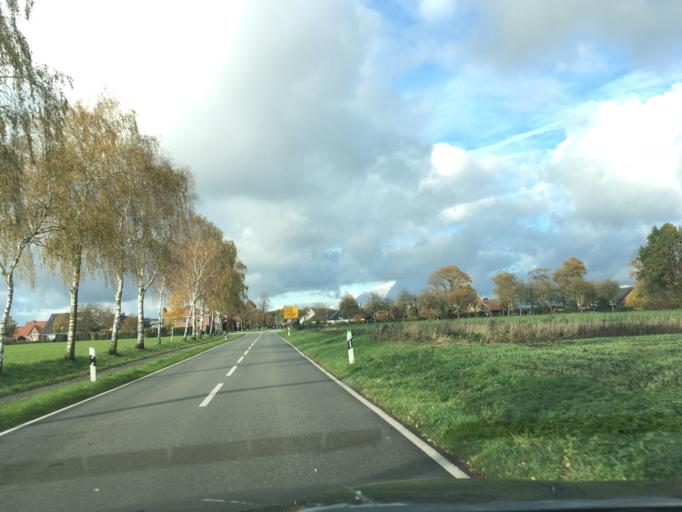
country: DE
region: North Rhine-Westphalia
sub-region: Regierungsbezirk Munster
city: Vreden
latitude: 52.0976
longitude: 6.8633
